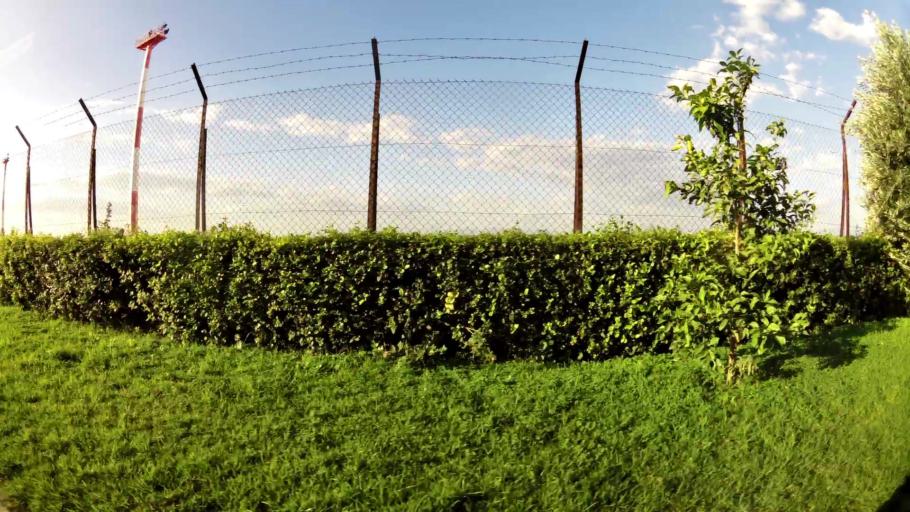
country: GR
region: Attica
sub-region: Nomarchia Athinas
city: Elliniko
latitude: 37.8818
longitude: 23.7427
